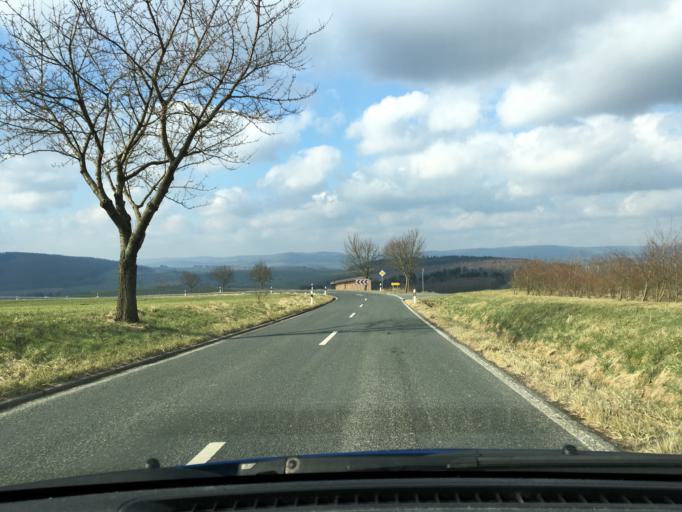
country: DE
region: Lower Saxony
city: Uslar
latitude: 51.6066
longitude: 9.6382
